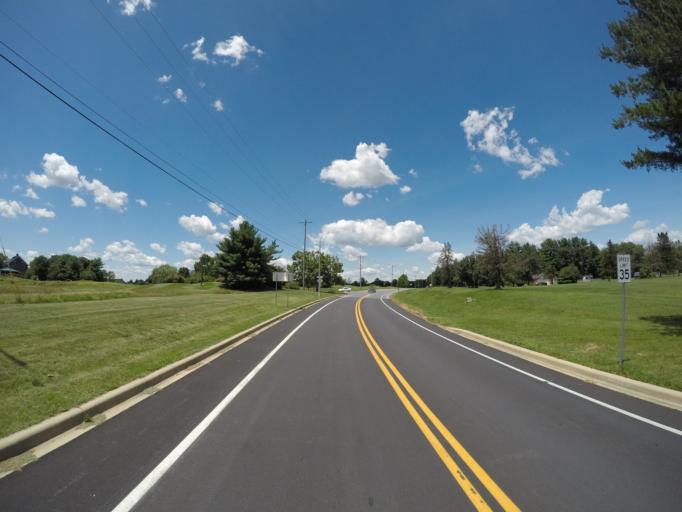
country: US
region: Delaware
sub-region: New Castle County
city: Middletown
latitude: 39.5043
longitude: -75.7503
